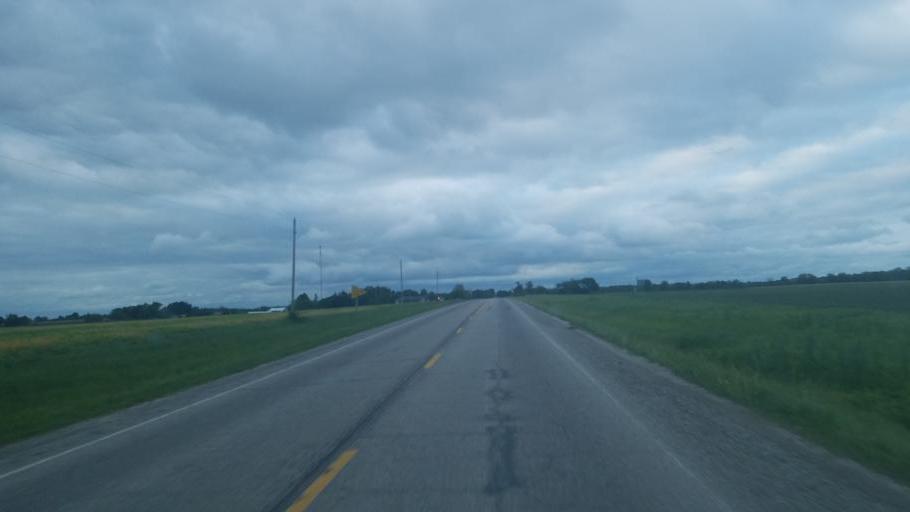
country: US
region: Iowa
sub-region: Decatur County
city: Lamoni
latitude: 40.5981
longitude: -93.9389
